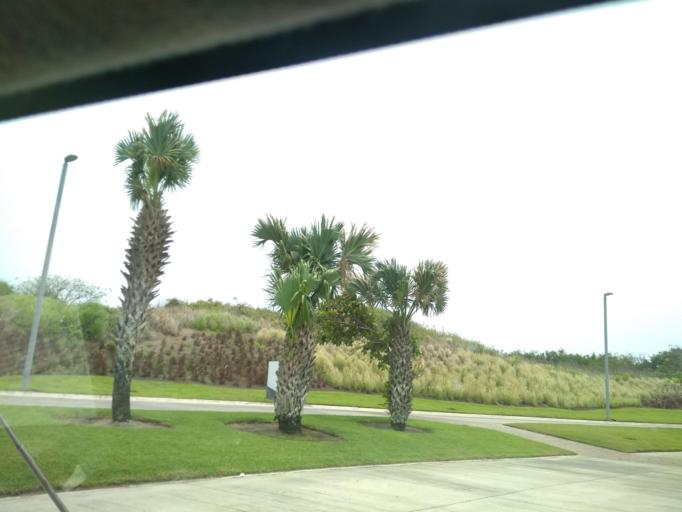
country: MX
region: Veracruz
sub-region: Alvarado
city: Playa de la Libertad
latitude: 19.0670
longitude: -96.0816
